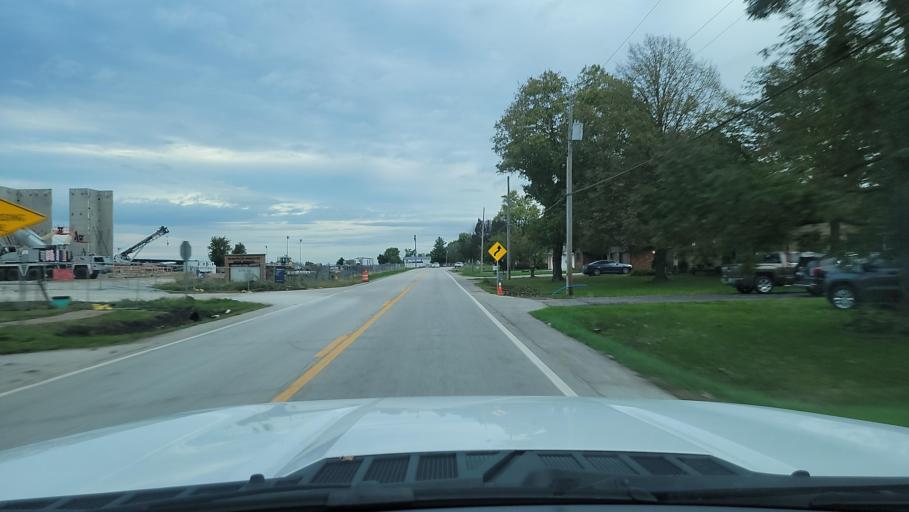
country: US
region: Illinois
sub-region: Schuyler County
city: Rushville
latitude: 40.1267
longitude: -90.5636
